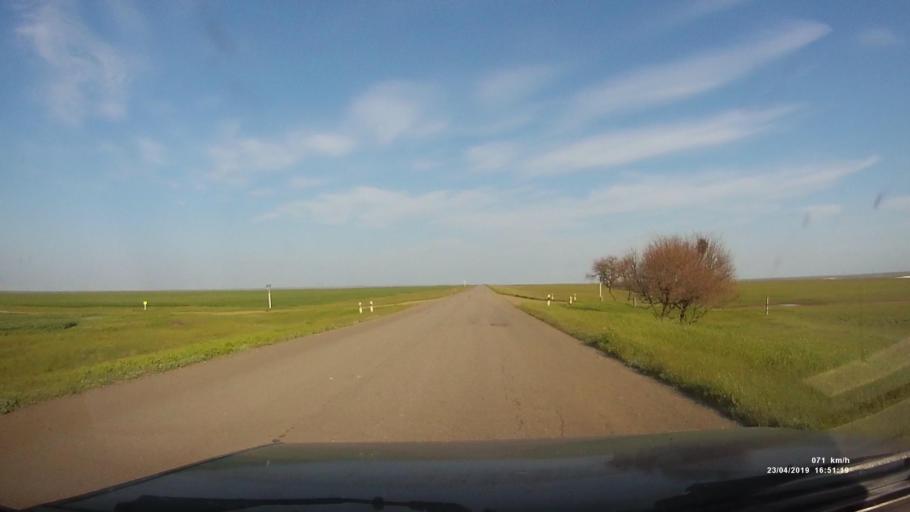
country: RU
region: Kalmykiya
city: Priyutnoye
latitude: 46.3235
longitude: 43.3043
